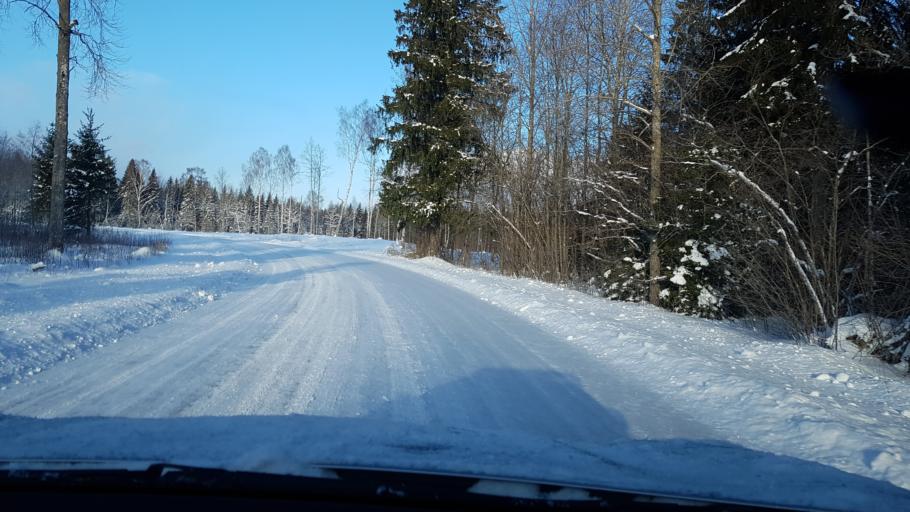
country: EE
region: Harju
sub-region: Nissi vald
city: Turba
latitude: 59.1172
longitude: 24.2218
